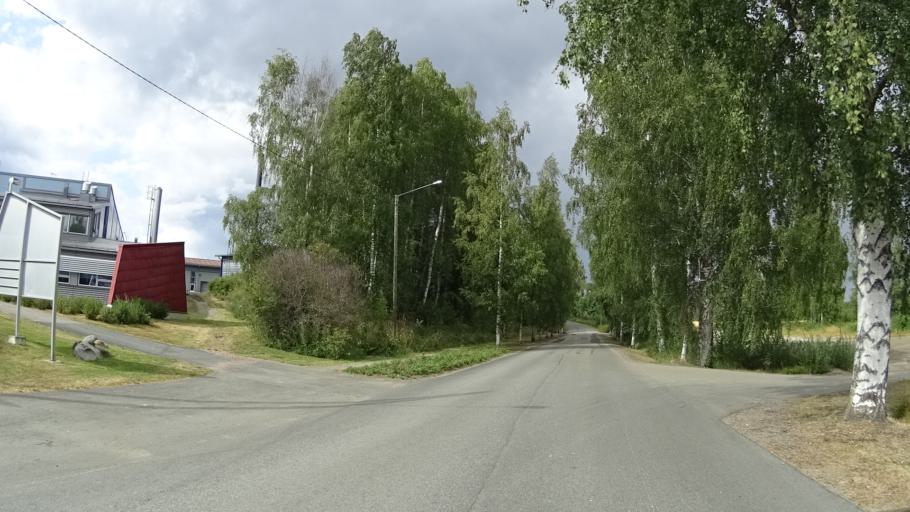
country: FI
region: Pirkanmaa
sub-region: Tampere
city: Kangasala
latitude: 61.4434
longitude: 24.1286
